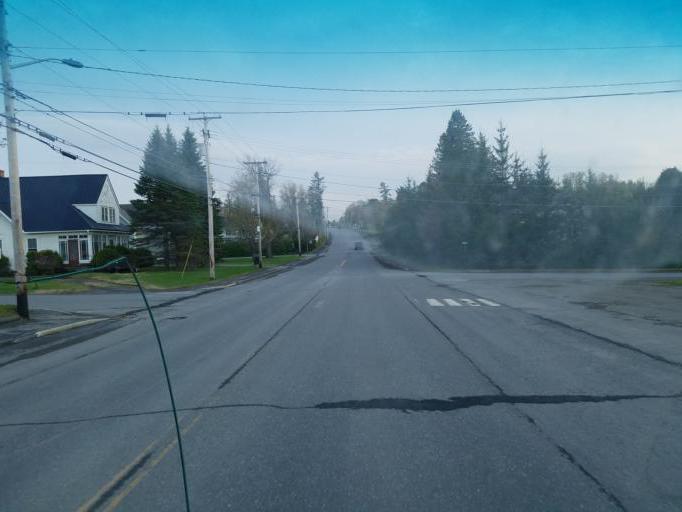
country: US
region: Maine
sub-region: Aroostook County
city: Caribou
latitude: 46.8556
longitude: -68.0111
